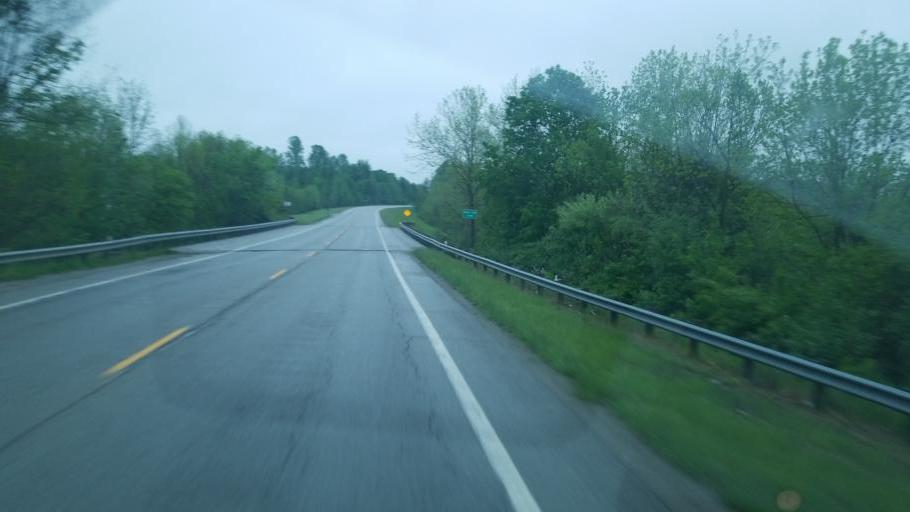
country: US
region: Ohio
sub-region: Highland County
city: Hillsboro
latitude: 39.1759
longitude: -83.6218
